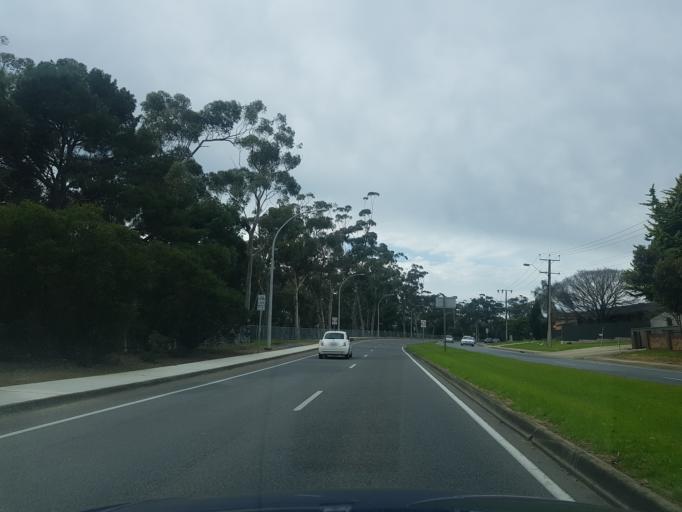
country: AU
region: South Australia
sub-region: Campbelltown
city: Athelstone
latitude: -34.8569
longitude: 138.6915
